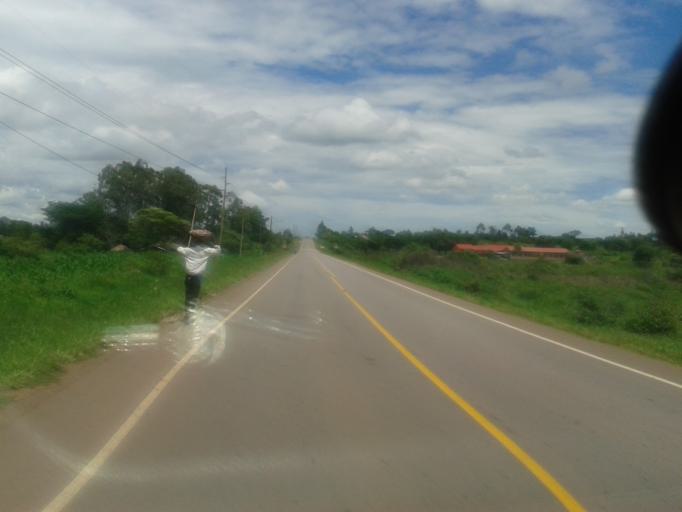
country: UG
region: Western Region
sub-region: Kiryandongo District
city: Kiryandongo
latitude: 1.7818
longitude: 32.0173
